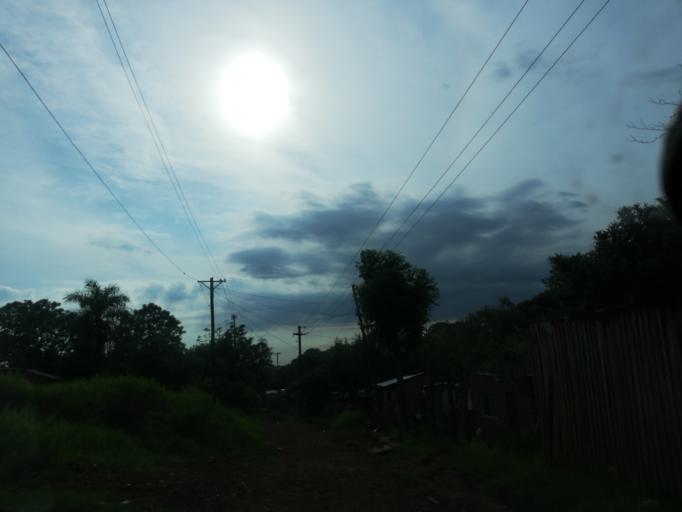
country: AR
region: Misiones
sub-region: Departamento de Capital
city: Posadas
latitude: -27.4202
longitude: -55.9170
